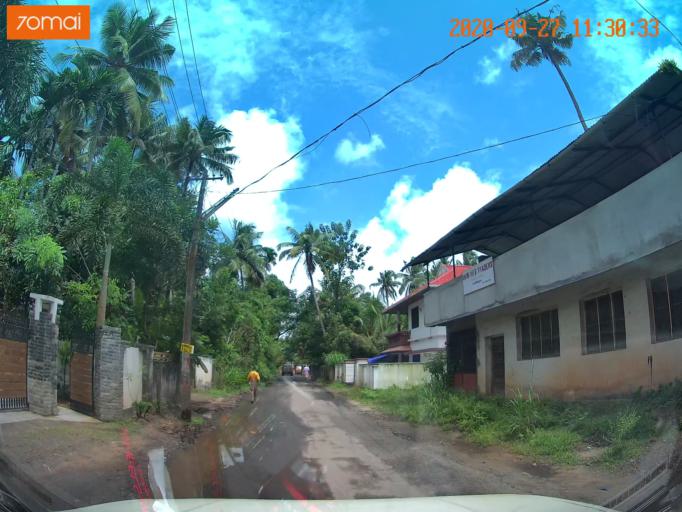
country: IN
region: Kerala
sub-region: Thrissur District
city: Thanniyam
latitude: 10.4195
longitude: 76.1340
